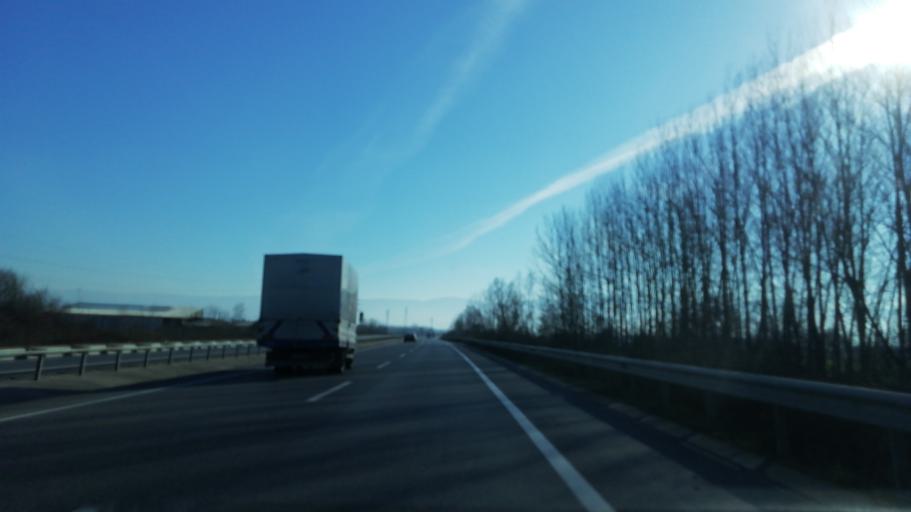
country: TR
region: Sakarya
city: Akyazi
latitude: 40.7393
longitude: 30.5645
